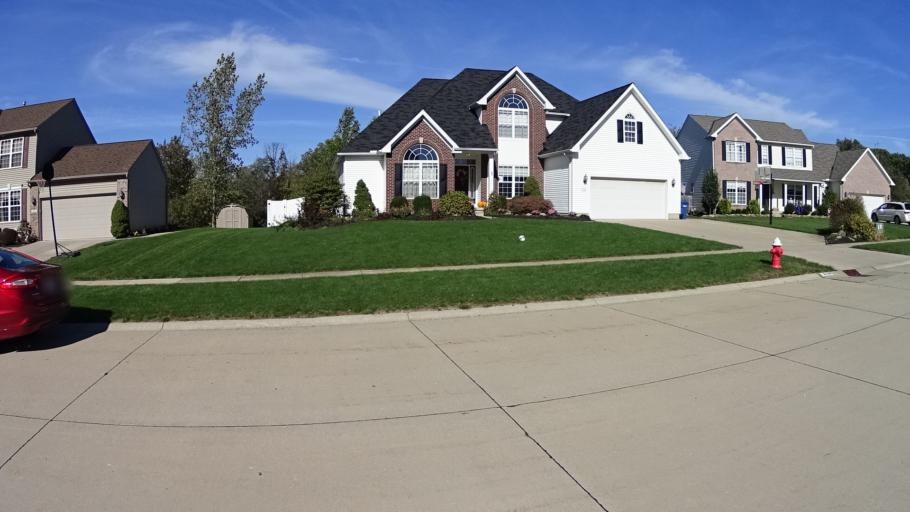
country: US
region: Ohio
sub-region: Lorain County
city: Amherst
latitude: 41.3869
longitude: -82.2384
